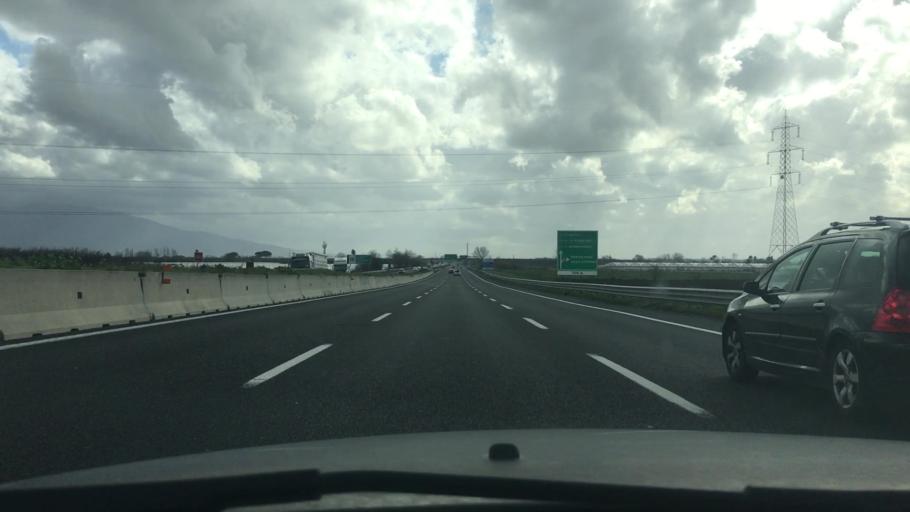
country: IT
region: Campania
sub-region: Provincia di Napoli
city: Pascarola
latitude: 40.9836
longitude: 14.3254
